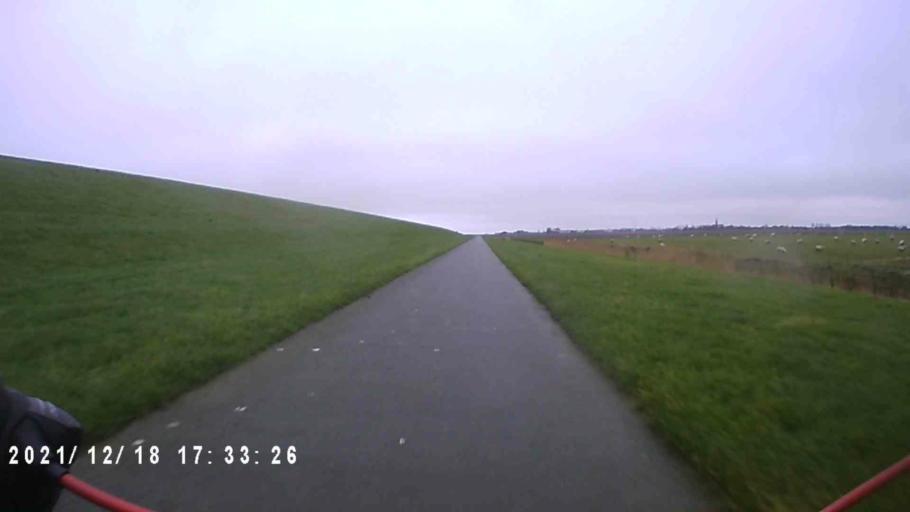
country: NL
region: Friesland
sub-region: Gemeente Dongeradeel
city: Holwerd
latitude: 53.3720
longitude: 5.8661
